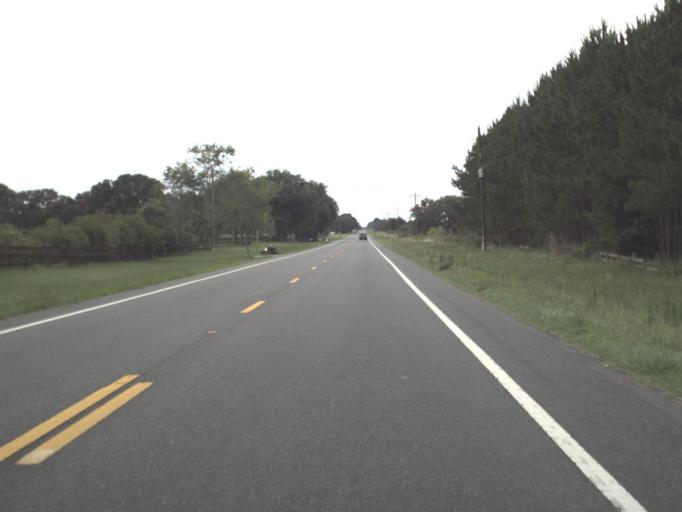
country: US
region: Florida
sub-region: Levy County
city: Williston
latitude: 29.3182
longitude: -82.4523
